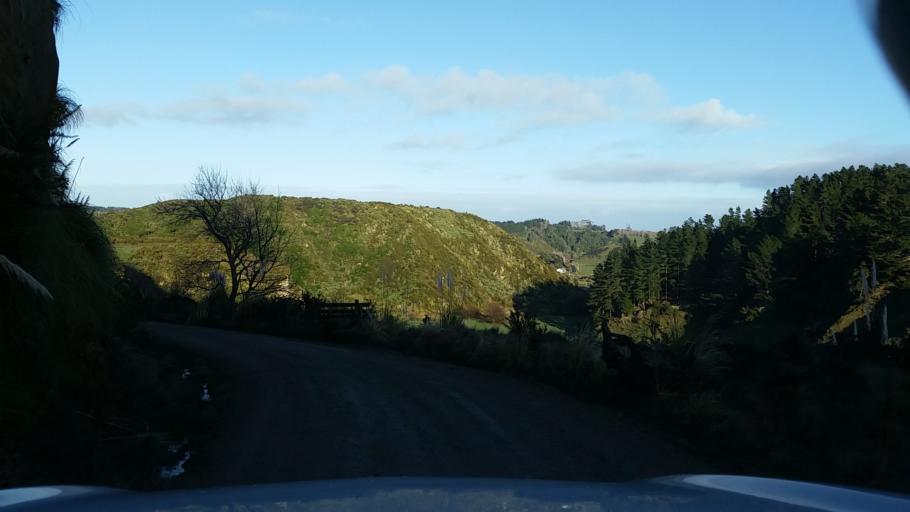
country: NZ
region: Taranaki
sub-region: South Taranaki District
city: Patea
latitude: -39.7572
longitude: 174.7395
